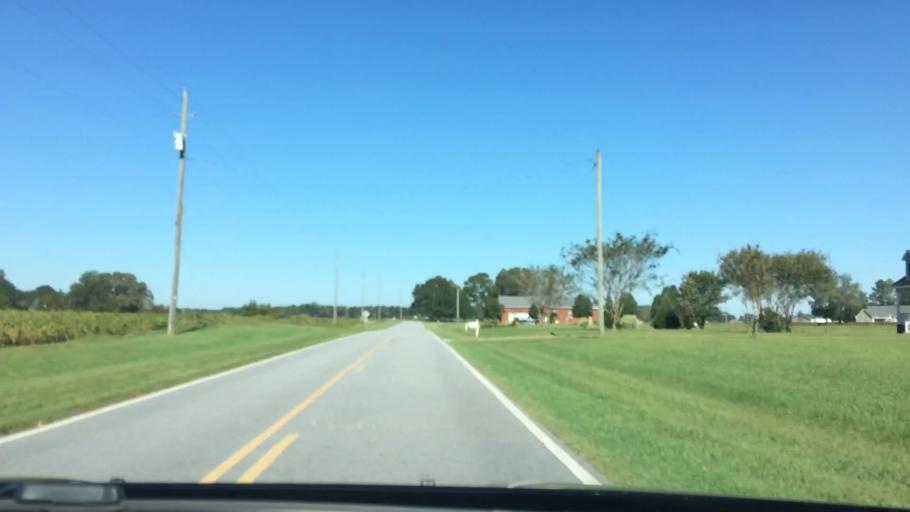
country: US
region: North Carolina
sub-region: Pitt County
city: Winterville
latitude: 35.5180
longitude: -77.4321
